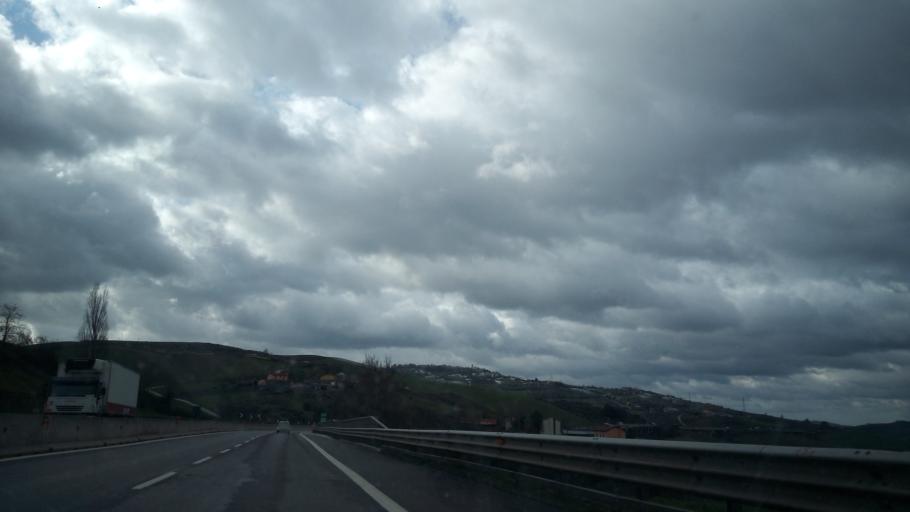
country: IT
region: Campania
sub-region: Provincia di Avellino
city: Flumeri
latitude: 41.0916
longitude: 15.1749
